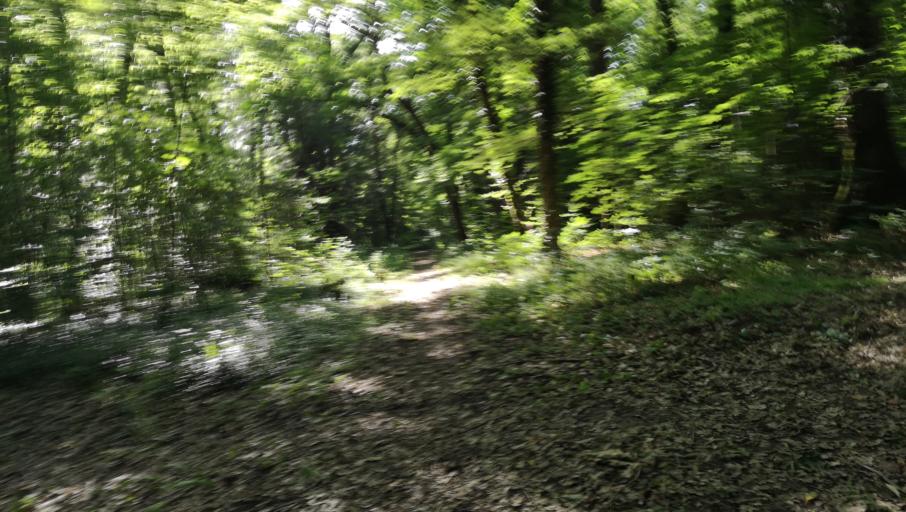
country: FR
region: Centre
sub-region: Departement du Loiret
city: Saint-Jean-de-Braye
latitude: 47.9216
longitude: 1.9823
